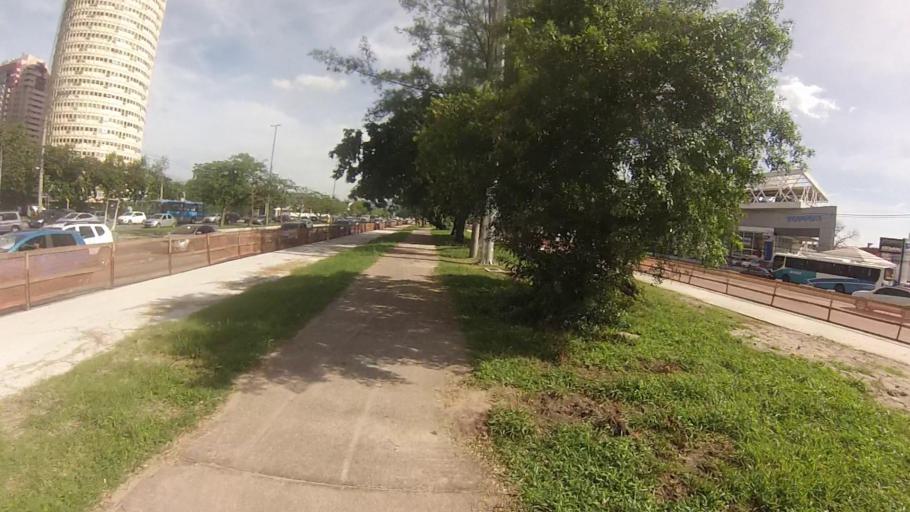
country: BR
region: Rio de Janeiro
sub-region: Rio De Janeiro
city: Rio de Janeiro
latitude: -23.0022
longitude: -43.3270
